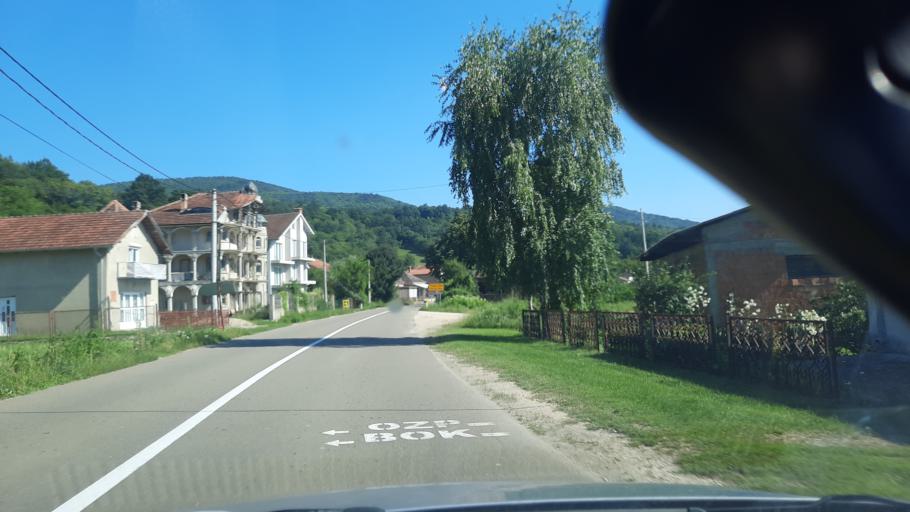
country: RS
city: Turija
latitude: 44.5228
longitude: 21.6397
